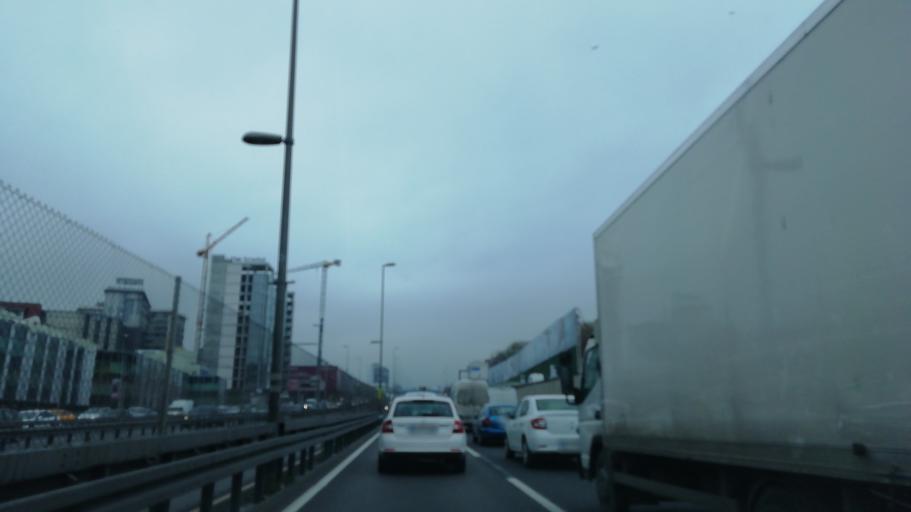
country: TR
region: Istanbul
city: guengoeren merter
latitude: 41.0084
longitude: 28.8987
